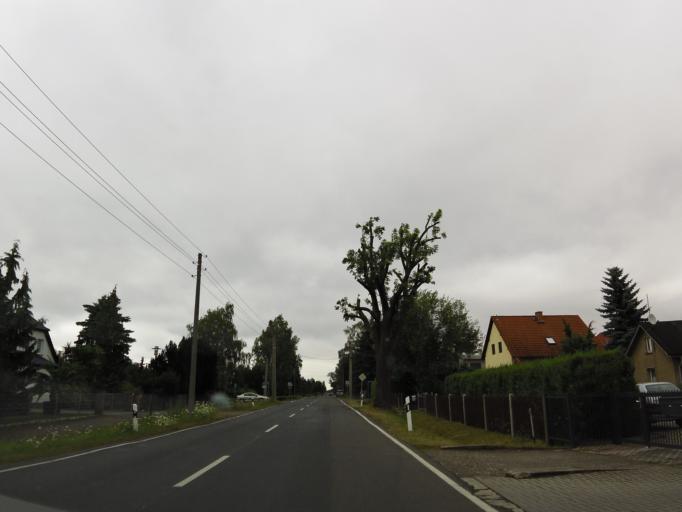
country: DE
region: Saxony
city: Markkleeberg
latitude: 51.2622
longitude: 12.4315
